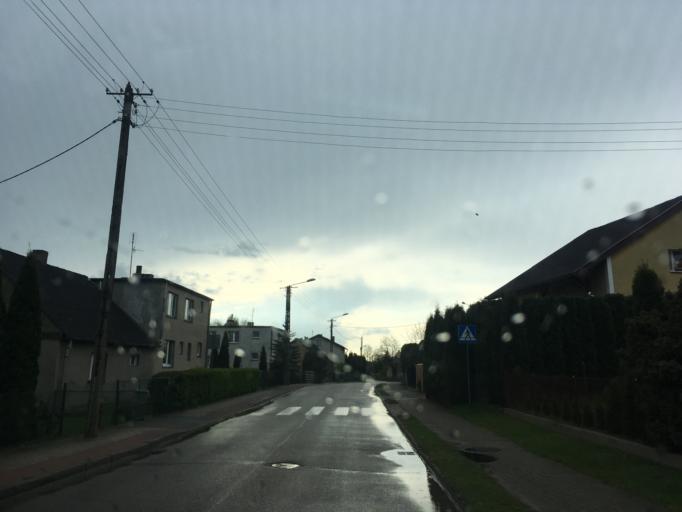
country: PL
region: Warmian-Masurian Voivodeship
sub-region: Powiat dzialdowski
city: Rybno
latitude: 53.3797
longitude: 19.9434
